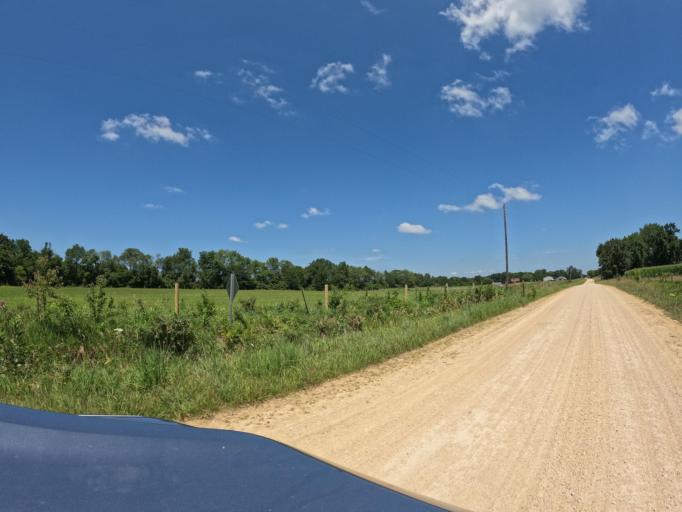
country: US
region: Iowa
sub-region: Clinton County
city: De Witt
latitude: 41.7614
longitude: -90.4326
